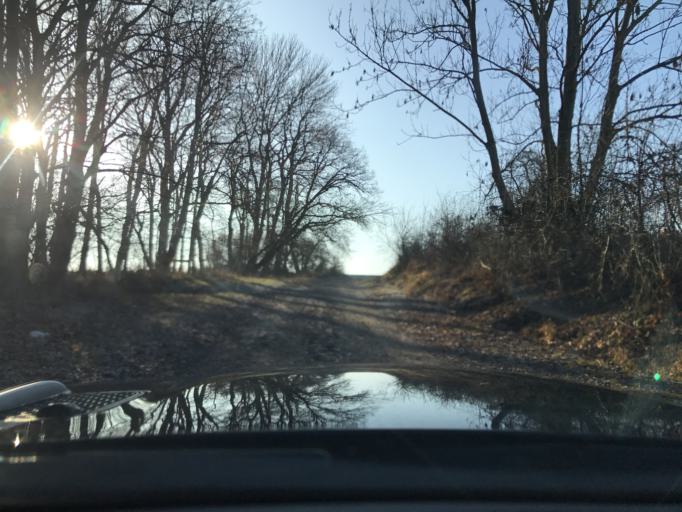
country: DE
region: Thuringia
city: Muehlhausen
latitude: 51.2389
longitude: 10.4458
